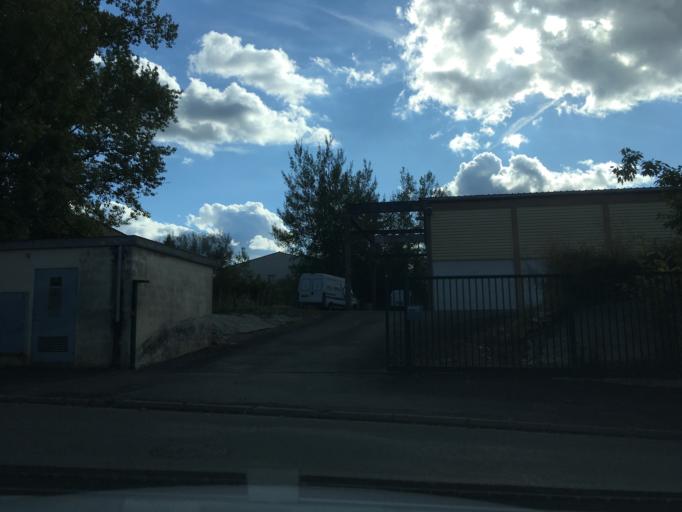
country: FR
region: Limousin
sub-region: Departement de la Correze
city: Malemort-sur-Correze
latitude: 45.1523
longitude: 1.5650
